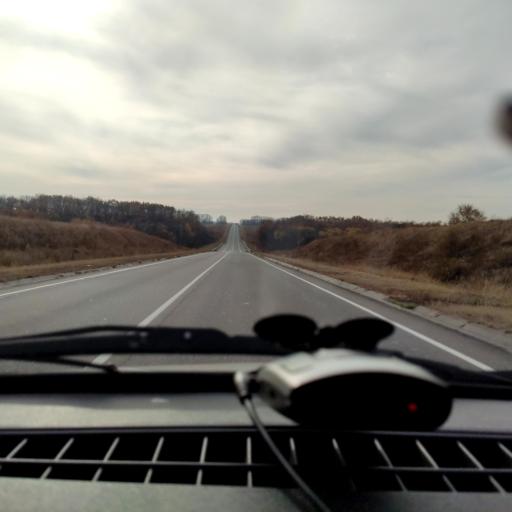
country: RU
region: Voronezj
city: Strelitsa
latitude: 51.5227
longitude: 38.9683
